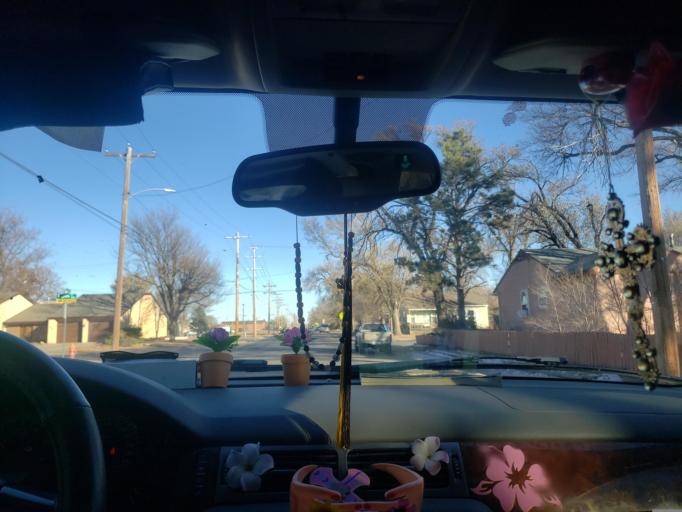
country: US
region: Kansas
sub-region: Finney County
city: Garden City
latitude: 37.9676
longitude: -100.8574
